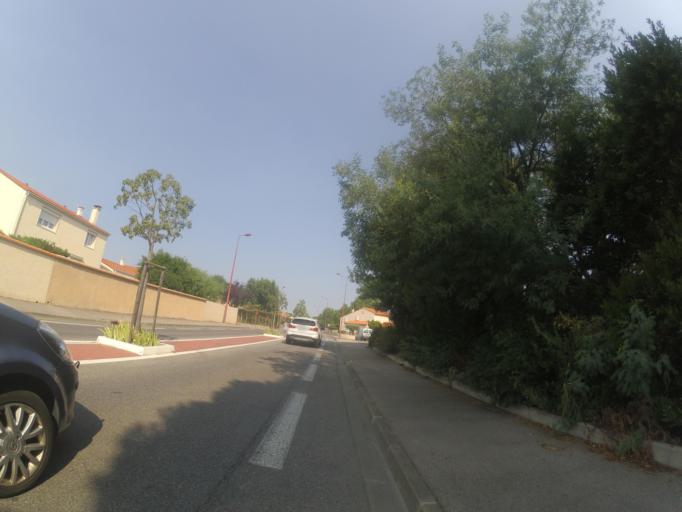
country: FR
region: Languedoc-Roussillon
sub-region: Departement des Pyrenees-Orientales
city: Toulouges
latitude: 42.6677
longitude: 2.8376
